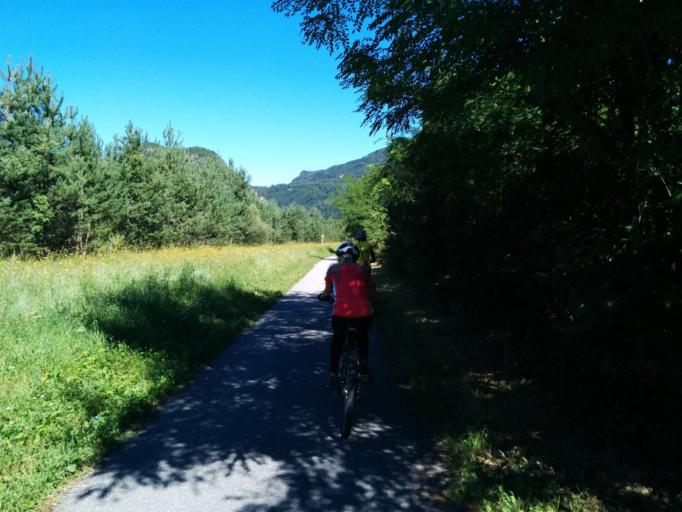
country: IT
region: Friuli Venezia Giulia
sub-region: Provincia di Udine
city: Villa Santina
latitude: 46.4143
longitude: 12.9081
